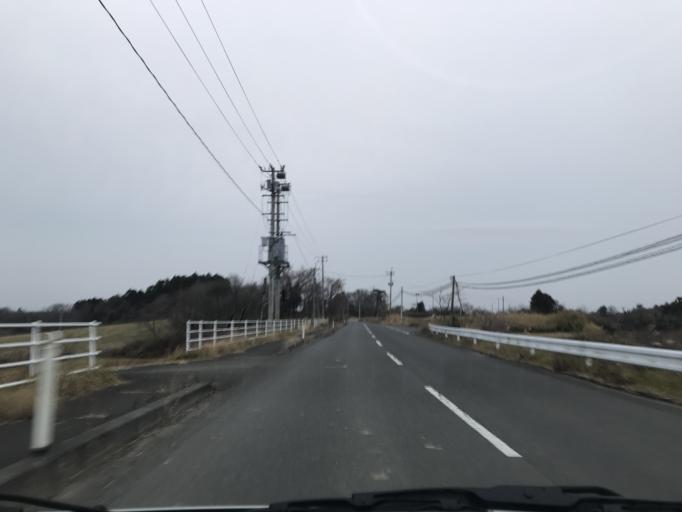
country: JP
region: Miyagi
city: Kogota
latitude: 38.6956
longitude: 141.0952
